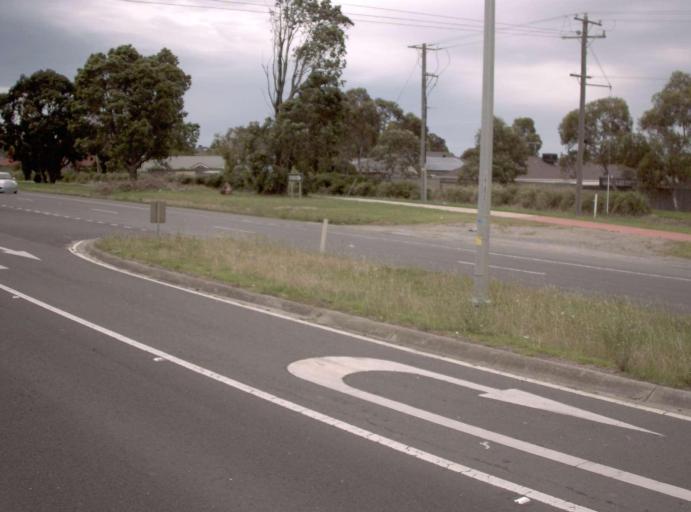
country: AU
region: Victoria
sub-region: Casey
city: Lynbrook
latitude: -38.0468
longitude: 145.2551
